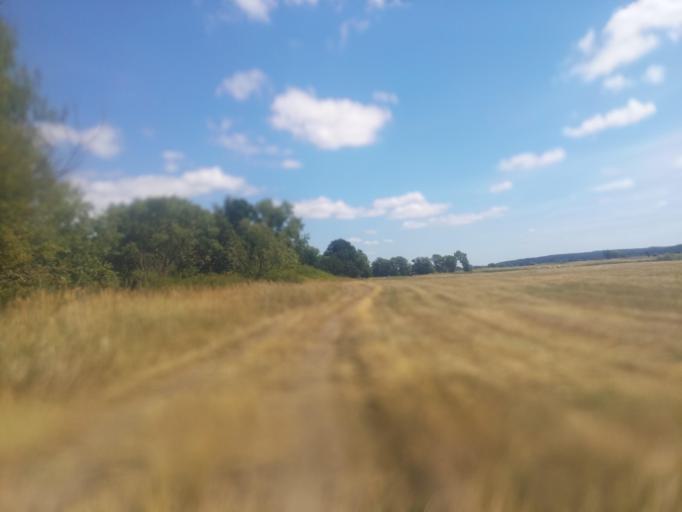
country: DE
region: Lower Saxony
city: Tosterglope
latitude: 53.2545
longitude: 10.8368
